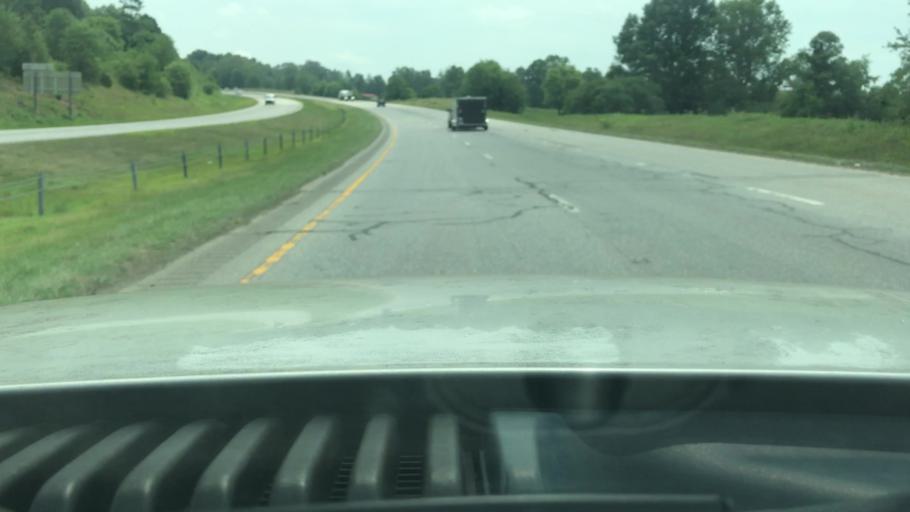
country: US
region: North Carolina
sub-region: Yadkin County
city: Jonesville
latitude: 36.1421
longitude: -80.8938
